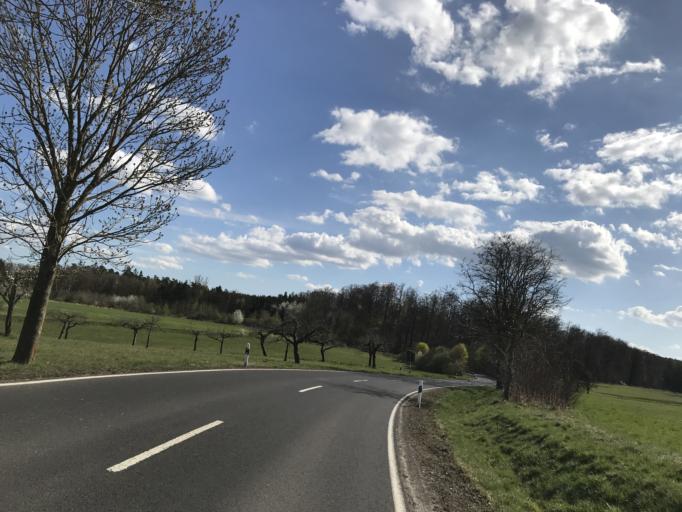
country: DE
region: Hesse
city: Beuern
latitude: 50.6560
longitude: 8.8182
